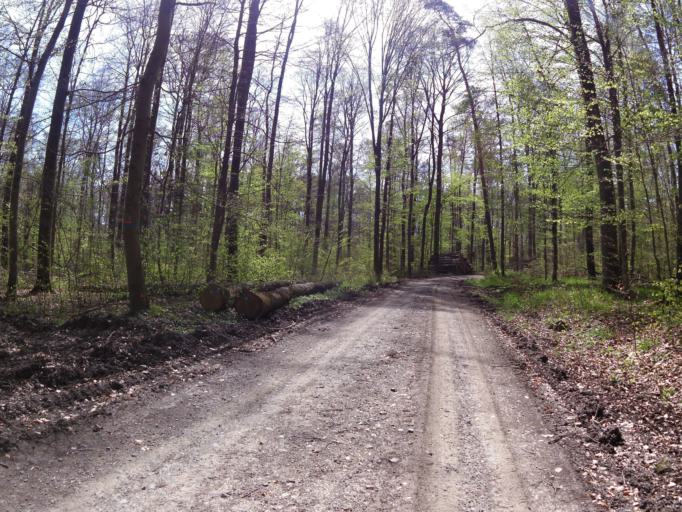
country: DE
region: Bavaria
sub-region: Regierungsbezirk Unterfranken
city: Rimpar
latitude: 49.8625
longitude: 9.9850
